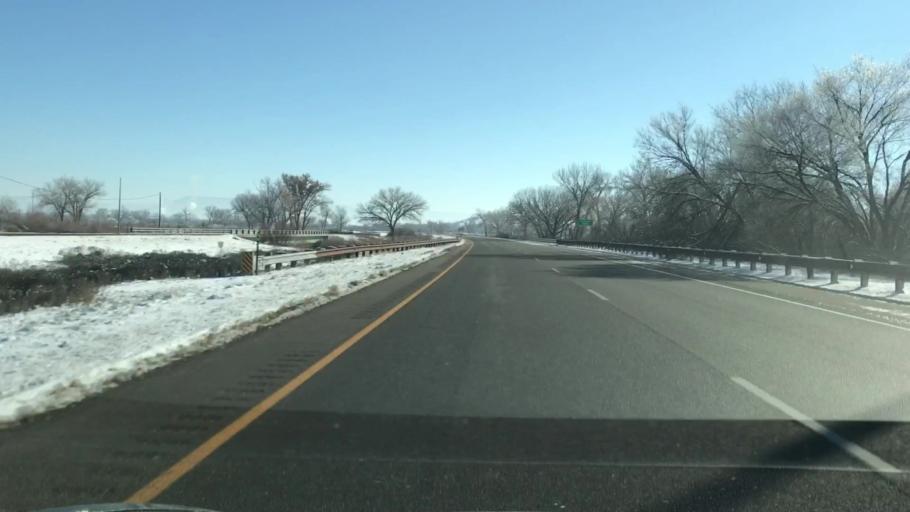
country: US
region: Colorado
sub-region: Mesa County
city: Loma
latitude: 39.1661
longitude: -108.7868
